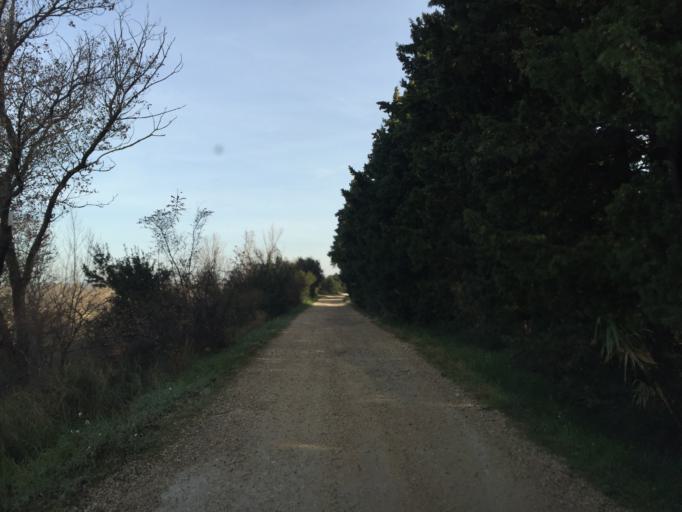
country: FR
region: Provence-Alpes-Cote d'Azur
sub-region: Departement du Vaucluse
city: Orange
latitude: 44.1589
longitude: 4.8133
